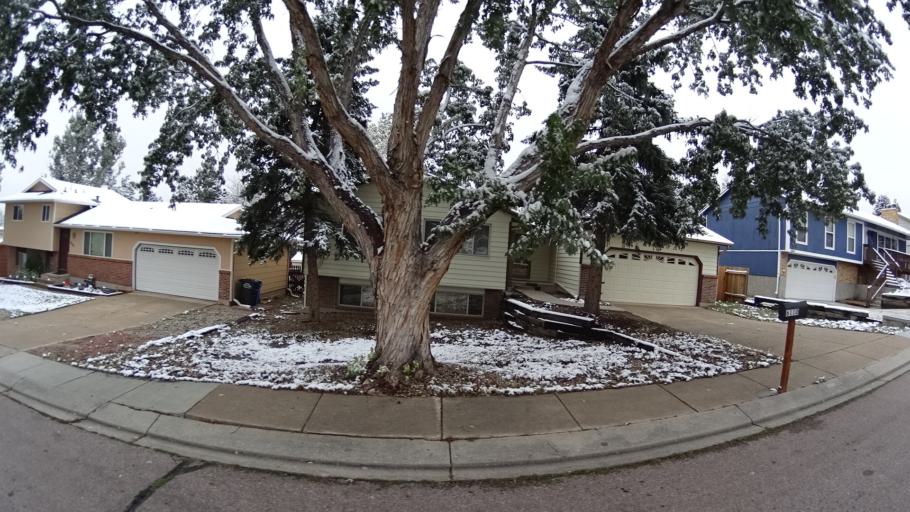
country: US
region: Colorado
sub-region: El Paso County
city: Colorado Springs
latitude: 38.9185
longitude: -104.7779
